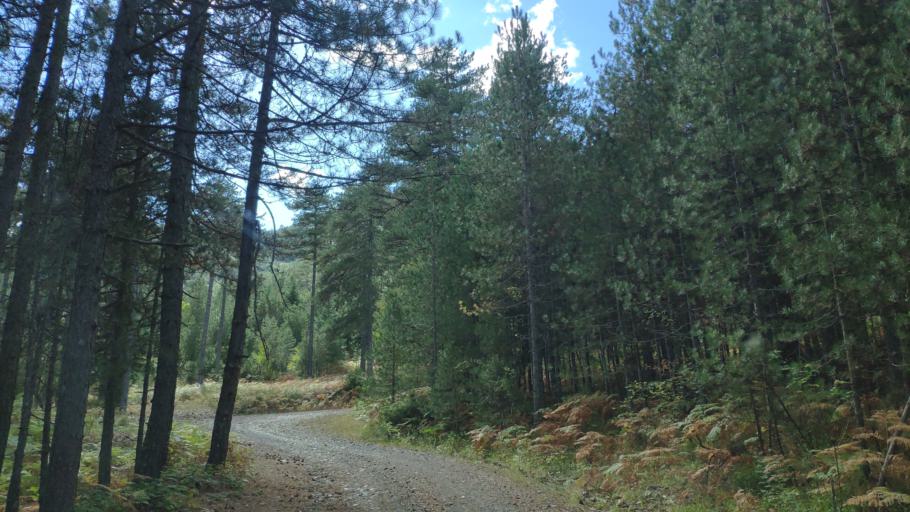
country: GR
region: Epirus
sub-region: Nomos Ioanninon
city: Metsovo
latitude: 39.8905
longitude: 21.2497
